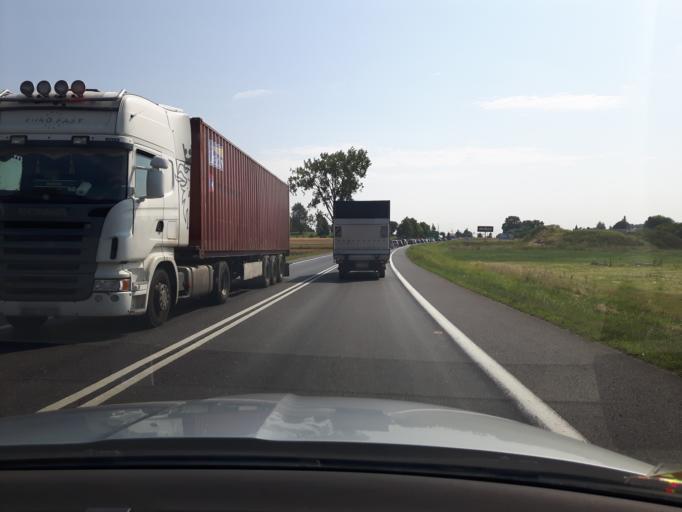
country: PL
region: Masovian Voivodeship
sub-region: Powiat mlawski
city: Mlawa
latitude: 53.1083
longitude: 20.4006
